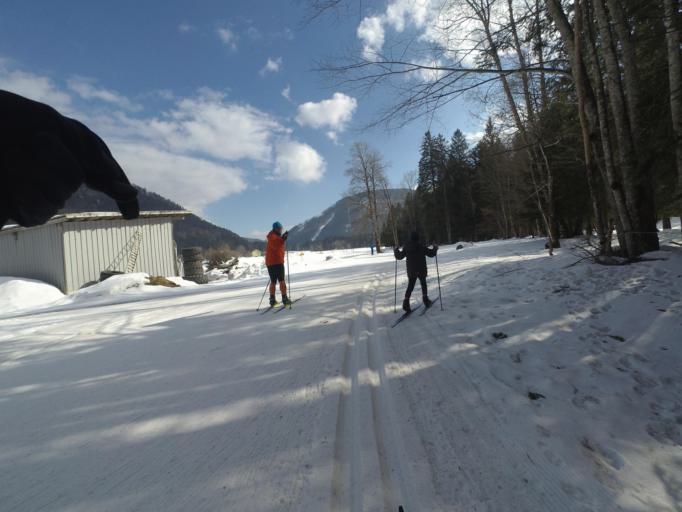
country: AT
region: Salzburg
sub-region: Politischer Bezirk Salzburg-Umgebung
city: Fuschl am See
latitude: 47.7724
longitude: 13.3060
